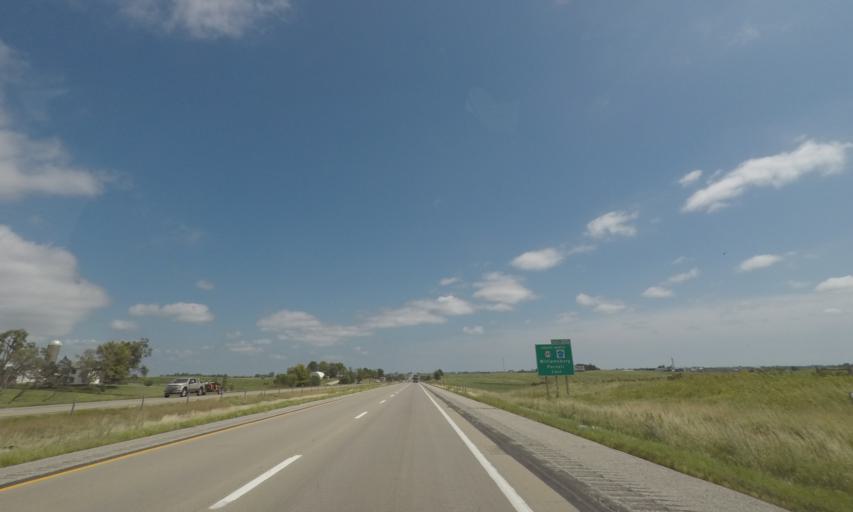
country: US
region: Iowa
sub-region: Iowa County
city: Williamsburg
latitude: 41.6871
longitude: -92.0327
